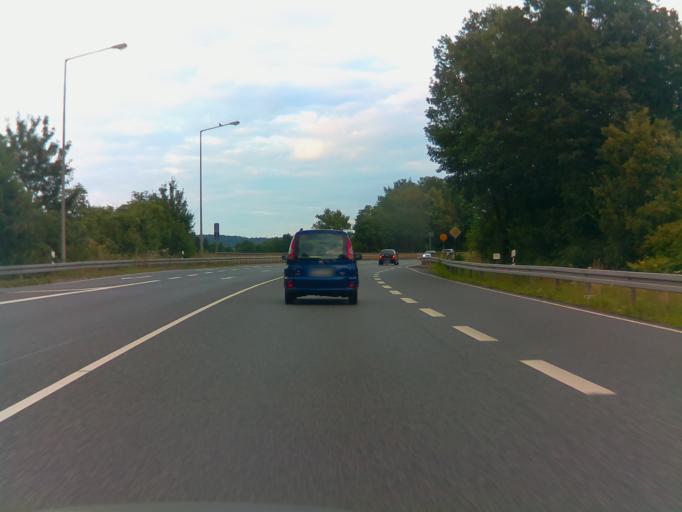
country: DE
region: Hesse
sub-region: Regierungsbezirk Kassel
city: Bad Hersfeld
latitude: 50.8544
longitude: 9.6895
